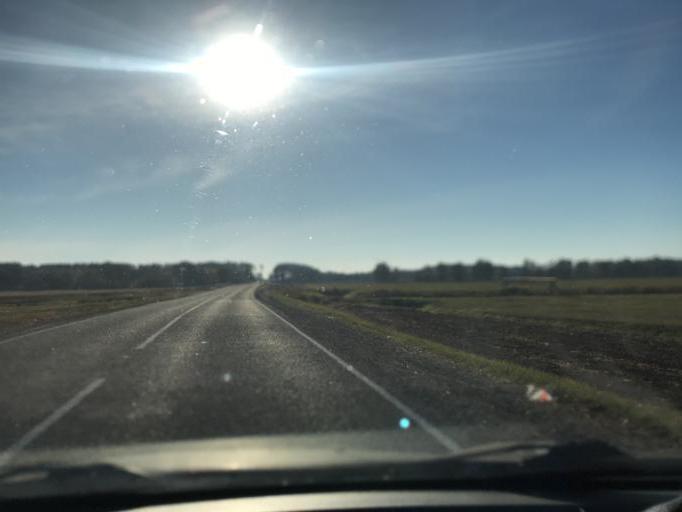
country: BY
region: Gomel
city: Brahin
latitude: 51.7732
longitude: 30.2935
